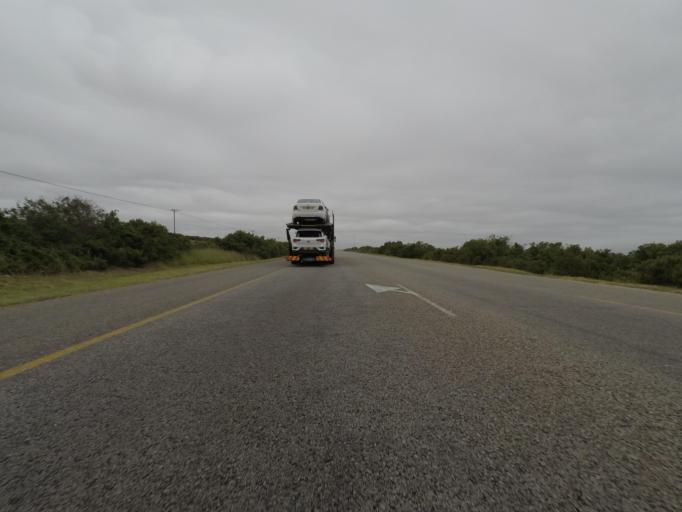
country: ZA
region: Eastern Cape
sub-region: Nelson Mandela Bay Metropolitan Municipality
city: Port Elizabeth
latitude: -33.6375
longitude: 25.8908
